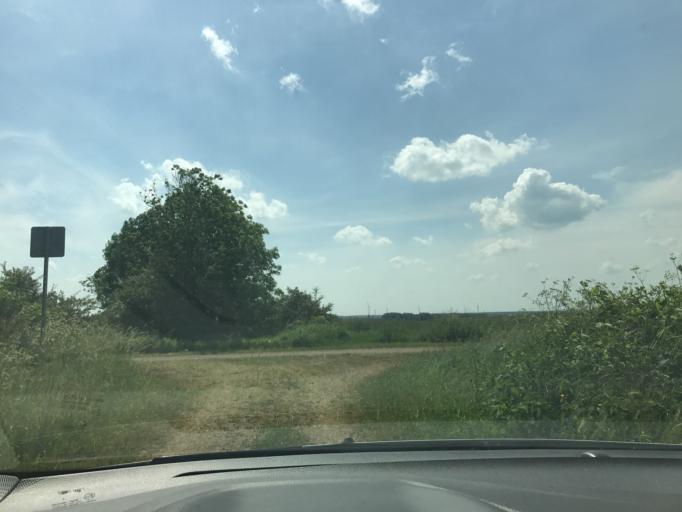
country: DE
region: Schleswig-Holstein
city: Ellhoft
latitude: 54.9316
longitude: 8.9603
